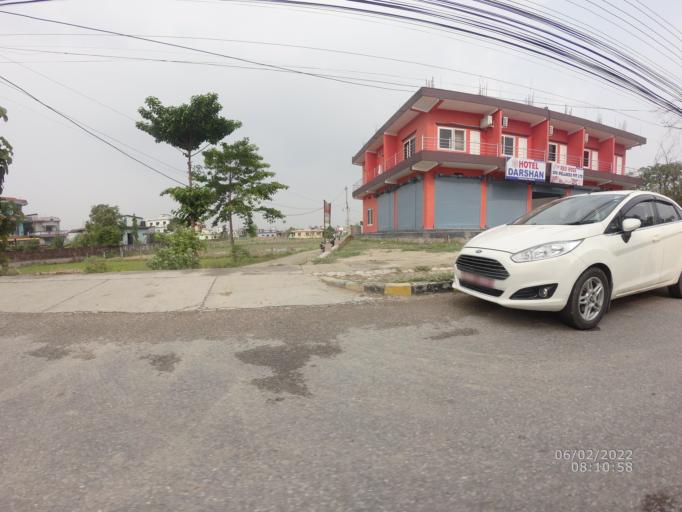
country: NP
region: Western Region
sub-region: Lumbini Zone
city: Bhairahawa
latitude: 27.4948
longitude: 83.4594
